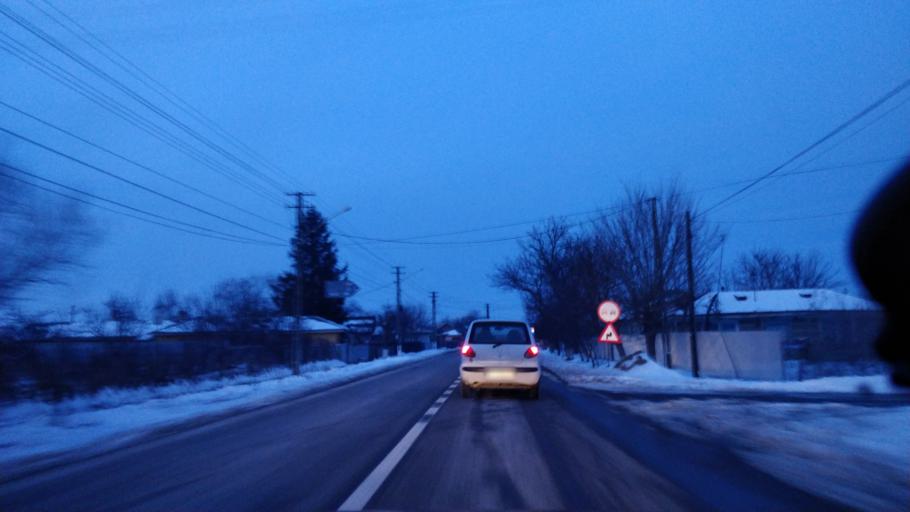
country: RO
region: Vrancea
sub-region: Comuna Nanesti
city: Nanesti
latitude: 45.5469
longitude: 27.4993
